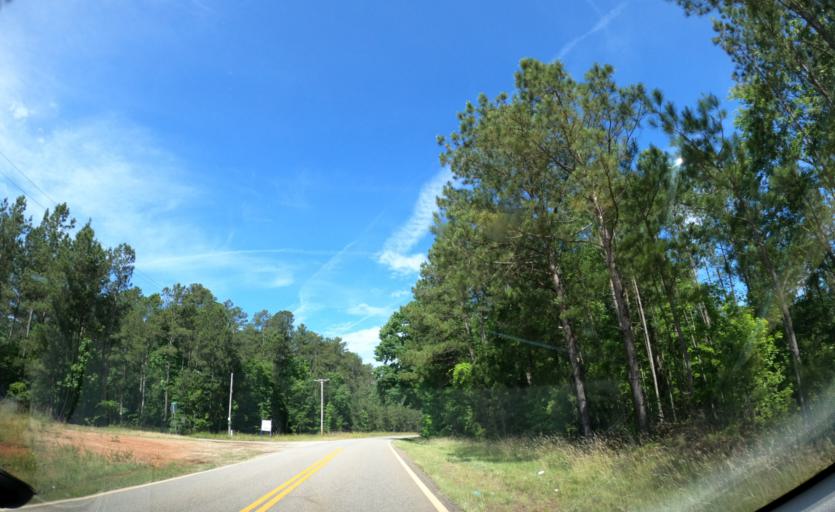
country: US
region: Georgia
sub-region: Elbert County
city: Elberton
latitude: 34.1417
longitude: -82.8085
